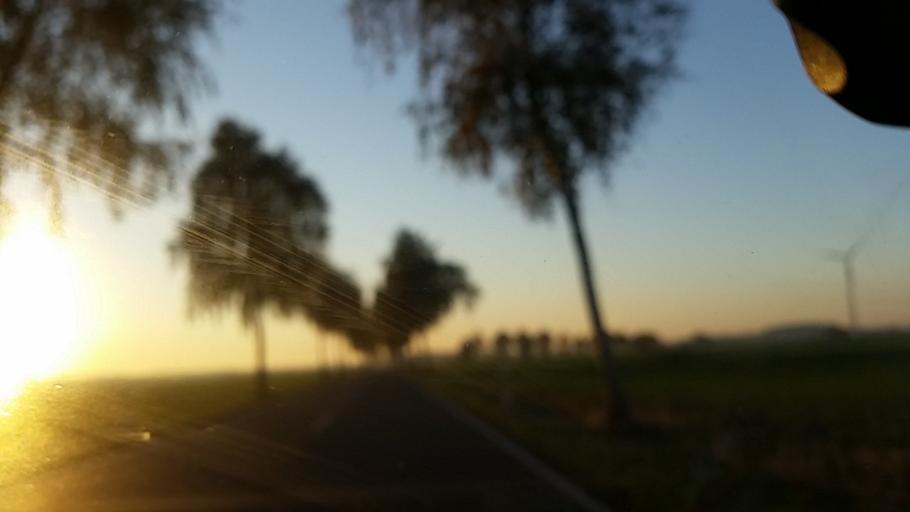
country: DE
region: Lower Saxony
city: Wittingen
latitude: 52.7544
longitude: 10.7182
